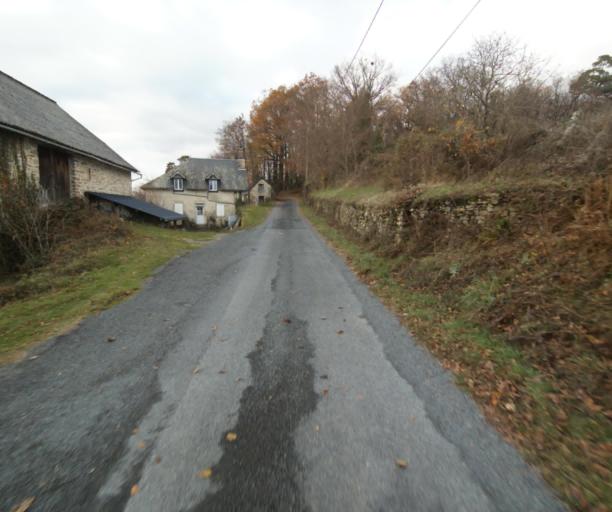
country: FR
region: Limousin
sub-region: Departement de la Correze
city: Sainte-Fortunade
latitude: 45.2160
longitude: 1.7887
